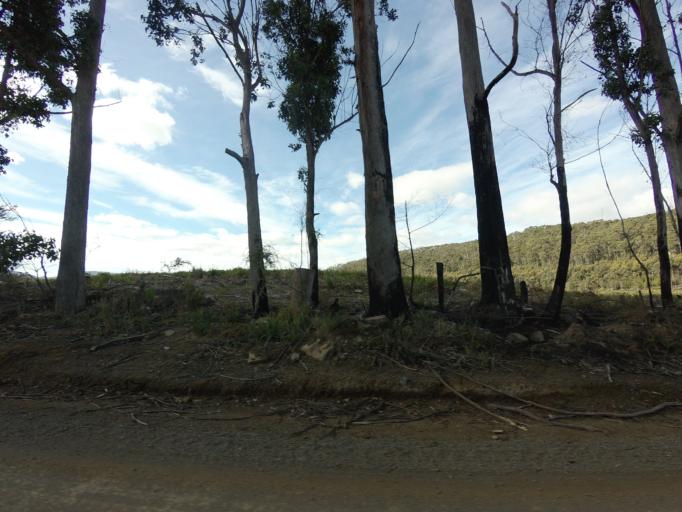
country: AU
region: Tasmania
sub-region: Clarence
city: Sandford
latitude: -43.1695
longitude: 147.7686
